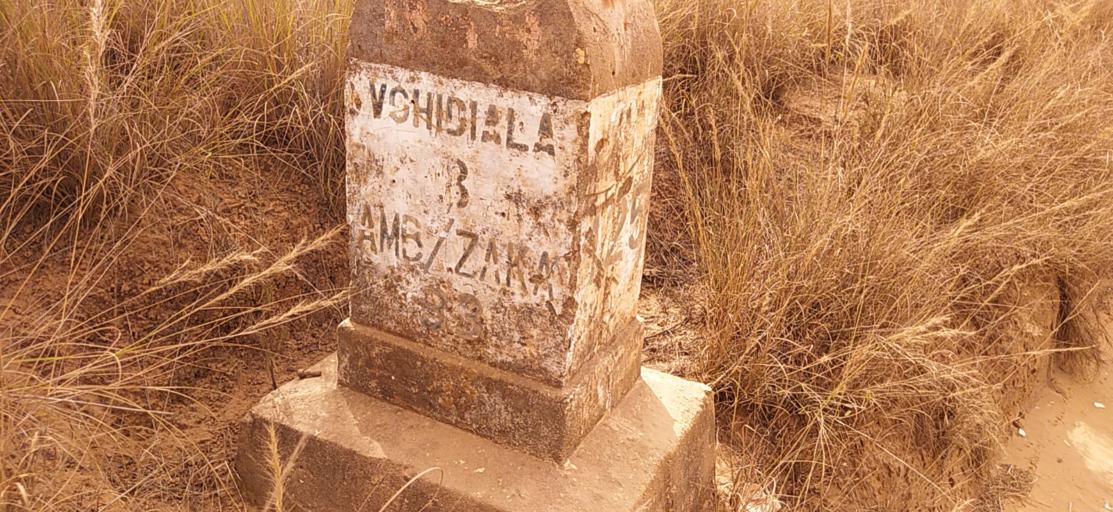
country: MG
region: Alaotra Mangoro
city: Ambatondrazaka
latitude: -17.9439
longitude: 48.2489
